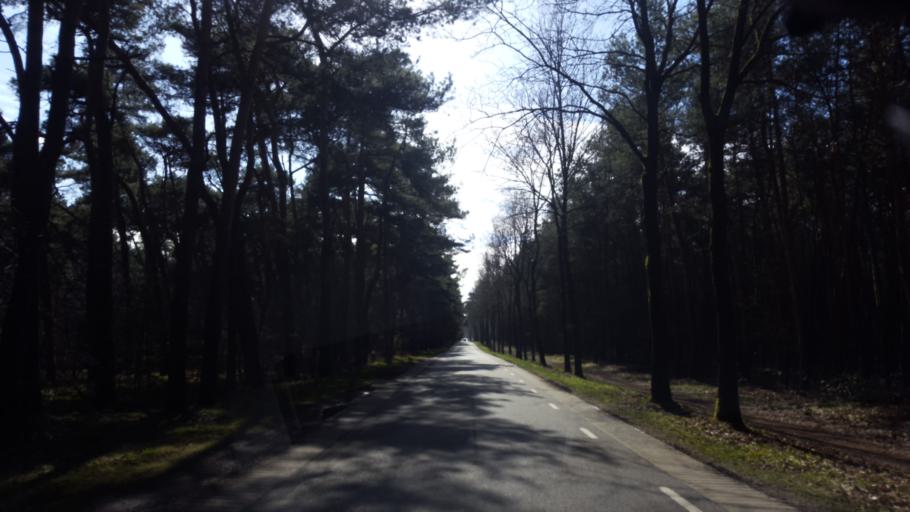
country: NL
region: Limburg
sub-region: Gemeente Weert
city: Weert
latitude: 51.2737
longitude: 5.6477
